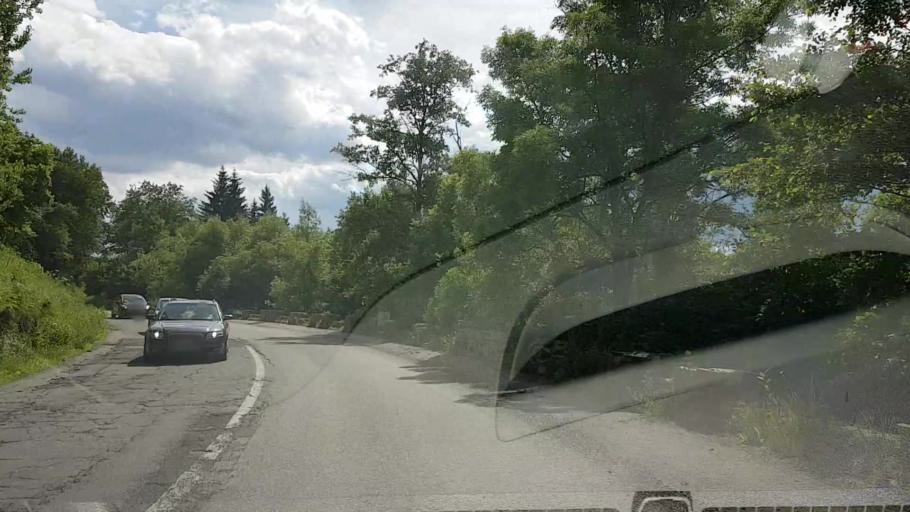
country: RO
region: Neamt
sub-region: Comuna Poiana Teiului
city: Poiana Teiului
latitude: 47.0766
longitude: 25.9652
